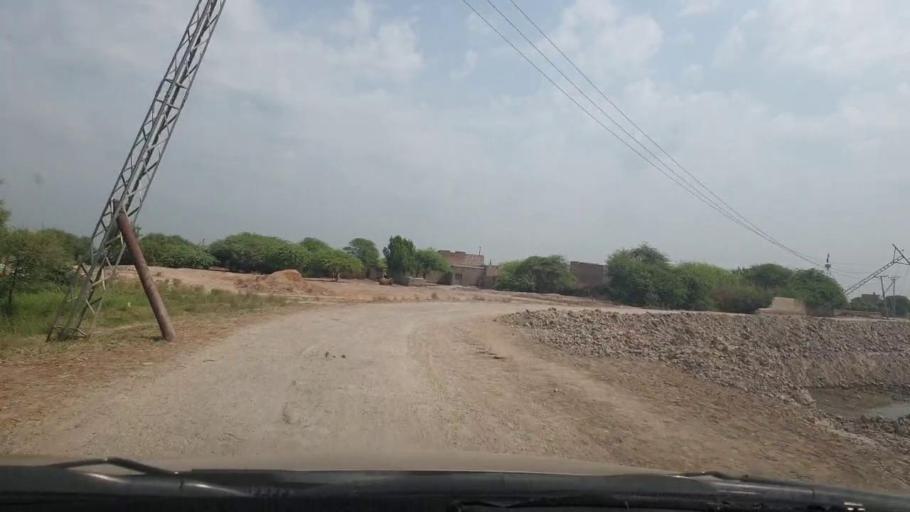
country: PK
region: Sindh
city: Larkana
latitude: 27.6787
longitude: 68.1917
